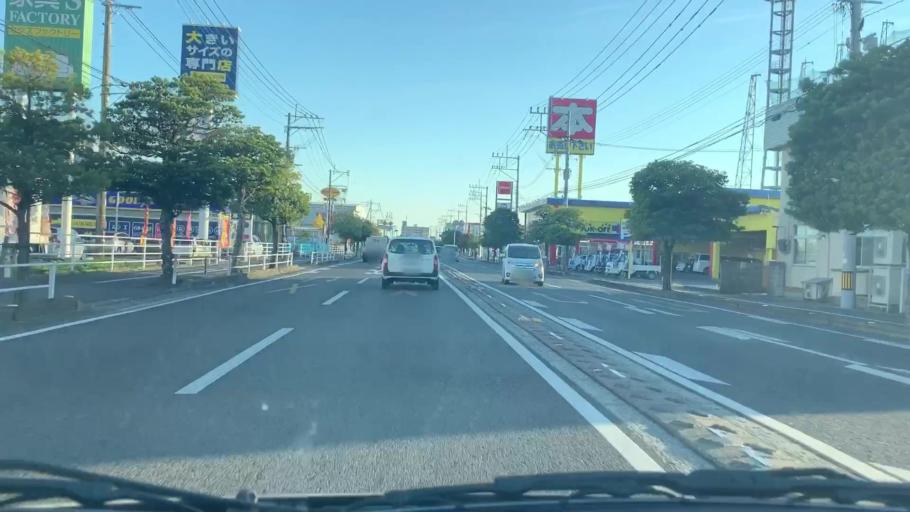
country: JP
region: Saga Prefecture
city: Saga-shi
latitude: 33.2658
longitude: 130.2719
